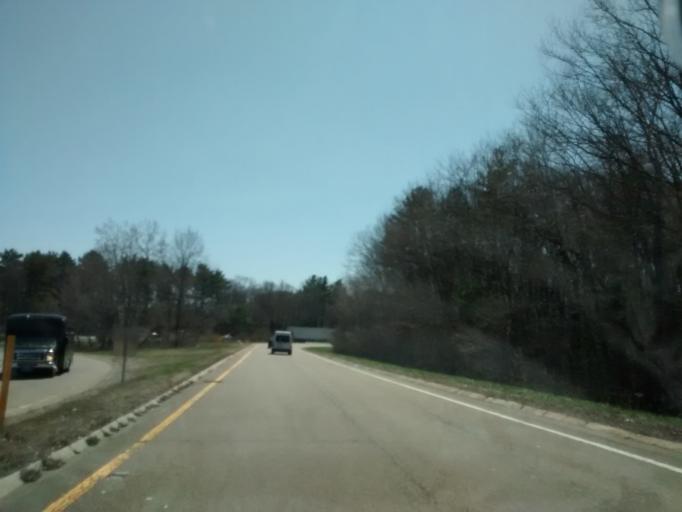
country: US
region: Massachusetts
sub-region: Norfolk County
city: Foxborough
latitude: 42.0264
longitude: -71.2609
